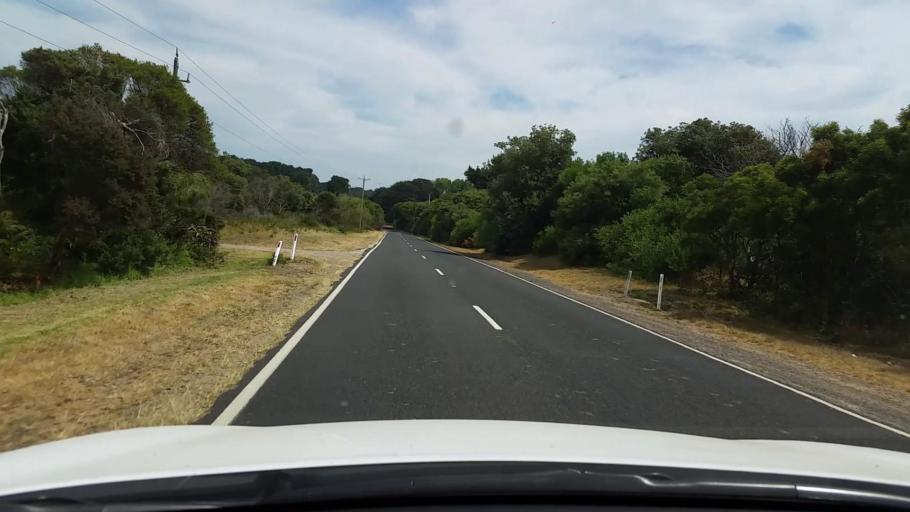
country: AU
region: Victoria
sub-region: Mornington Peninsula
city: Saint Andrews Beach
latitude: -38.4682
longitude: 144.9188
